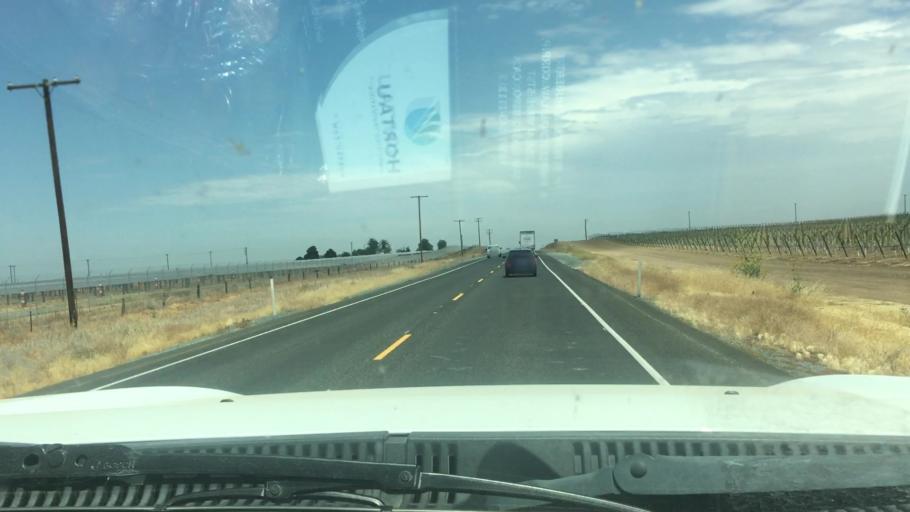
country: US
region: California
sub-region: Tulare County
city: Richgrove
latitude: 35.8444
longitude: -119.0537
